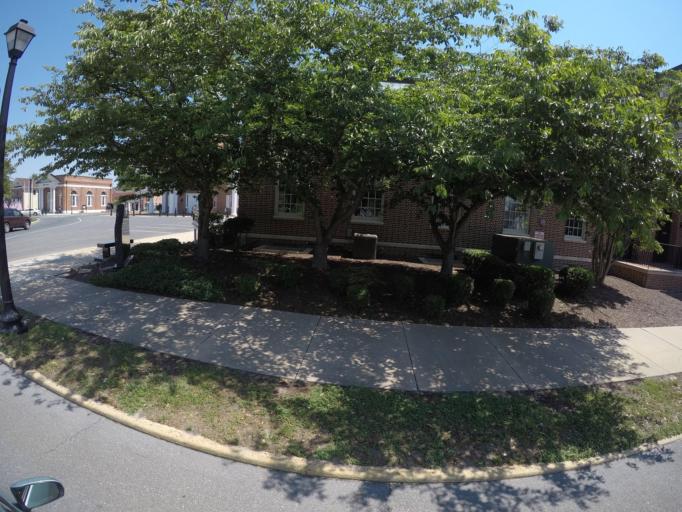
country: US
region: Delaware
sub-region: Sussex County
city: Georgetown
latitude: 38.6898
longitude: -75.3851
